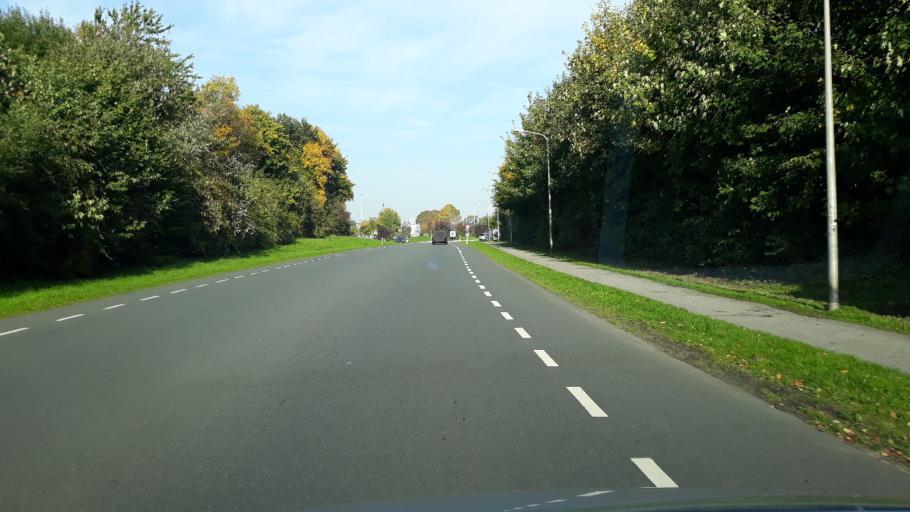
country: DE
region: Schleswig-Holstein
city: Schleswig
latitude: 54.5292
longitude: 9.5723
